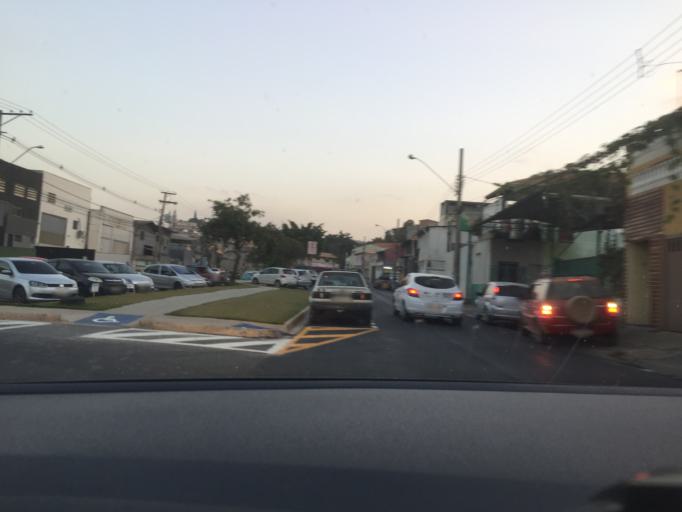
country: BR
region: Sao Paulo
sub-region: Varzea Paulista
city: Varzea Paulista
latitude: -23.2232
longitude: -46.8416
